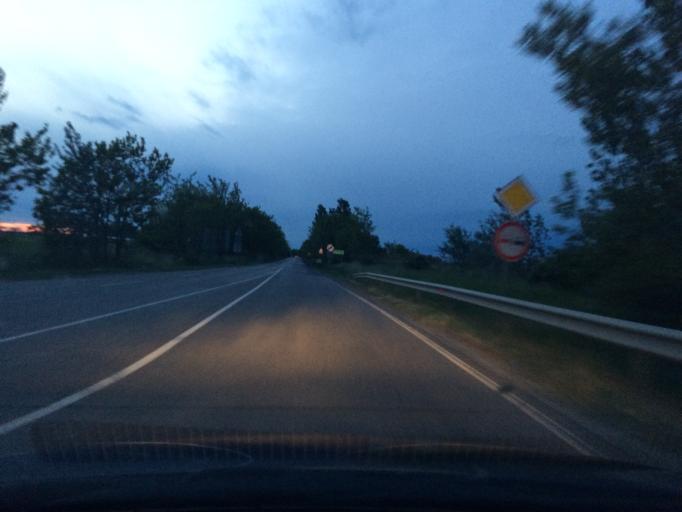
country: HU
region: Hajdu-Bihar
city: Hajdunanas
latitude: 47.8857
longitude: 21.4141
